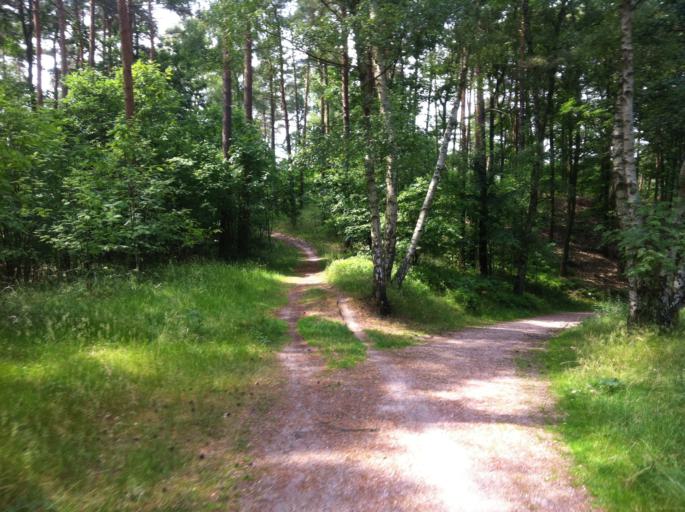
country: DE
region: Lower Saxony
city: Neu Wulmstorf
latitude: 53.4561
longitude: 9.8801
